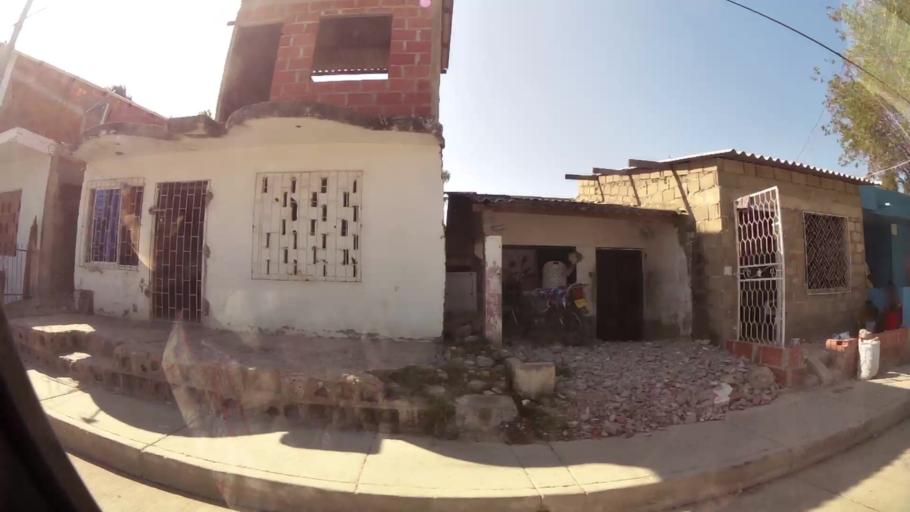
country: CO
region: Bolivar
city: Cartagena
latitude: 10.4140
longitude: -75.5115
